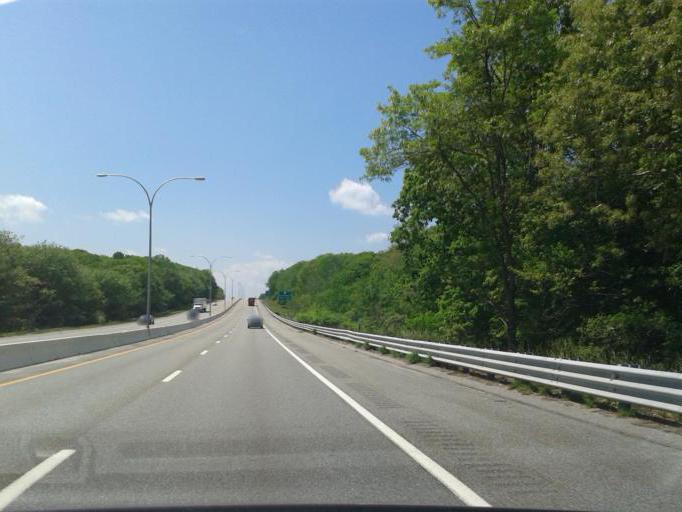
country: US
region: Rhode Island
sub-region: Washington County
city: North Kingstown
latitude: 41.5288
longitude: -71.4439
